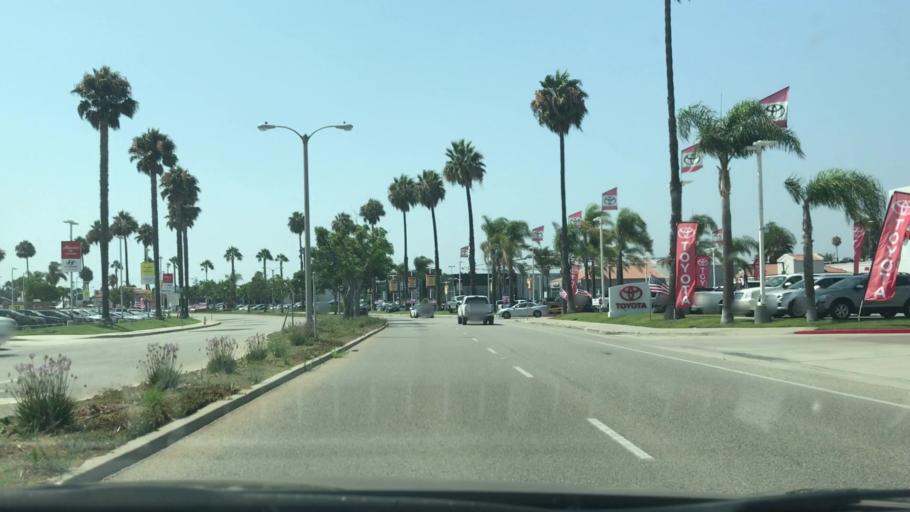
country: US
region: California
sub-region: Ventura County
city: El Rio
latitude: 34.2279
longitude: -119.1528
